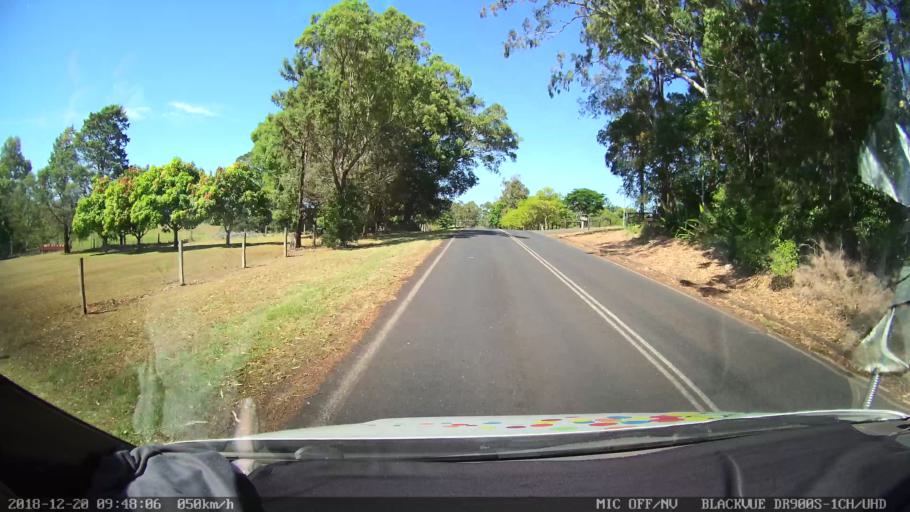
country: AU
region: New South Wales
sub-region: Lismore Municipality
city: Lismore
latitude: -28.7679
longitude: 153.2935
